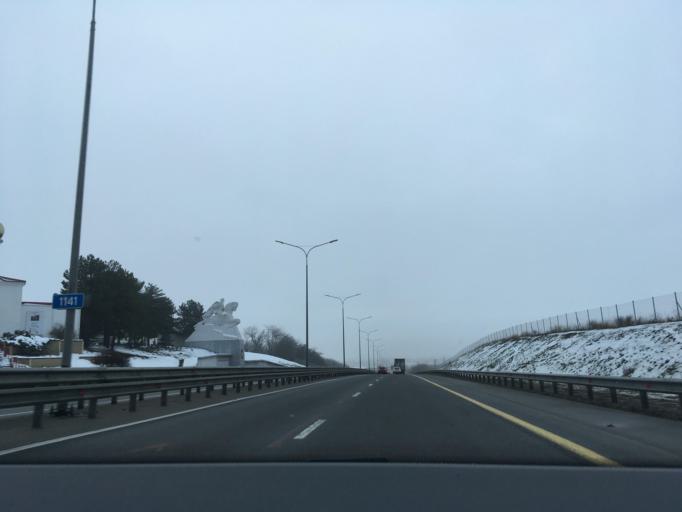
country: RU
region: Krasnodarskiy
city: Kushchevskaya
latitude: 46.5965
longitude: 39.6640
